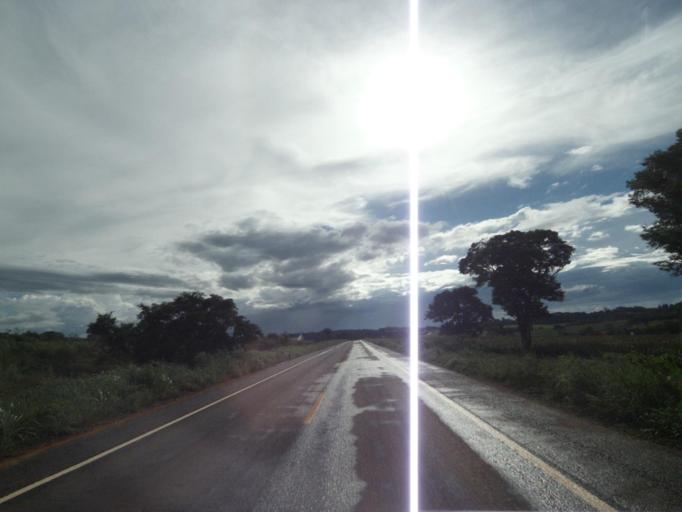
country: BR
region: Goias
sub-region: Jaragua
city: Jaragua
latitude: -15.9054
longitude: -49.5494
